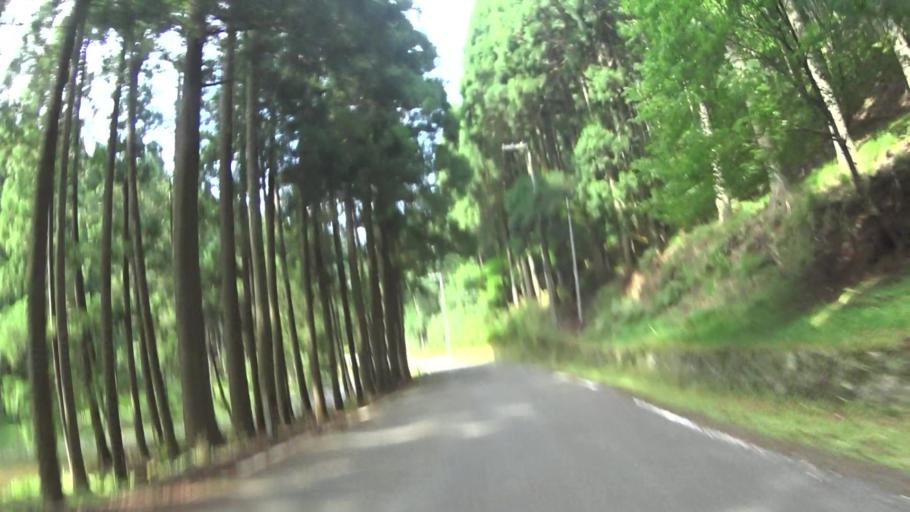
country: JP
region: Fukui
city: Obama
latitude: 35.3290
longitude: 135.6462
